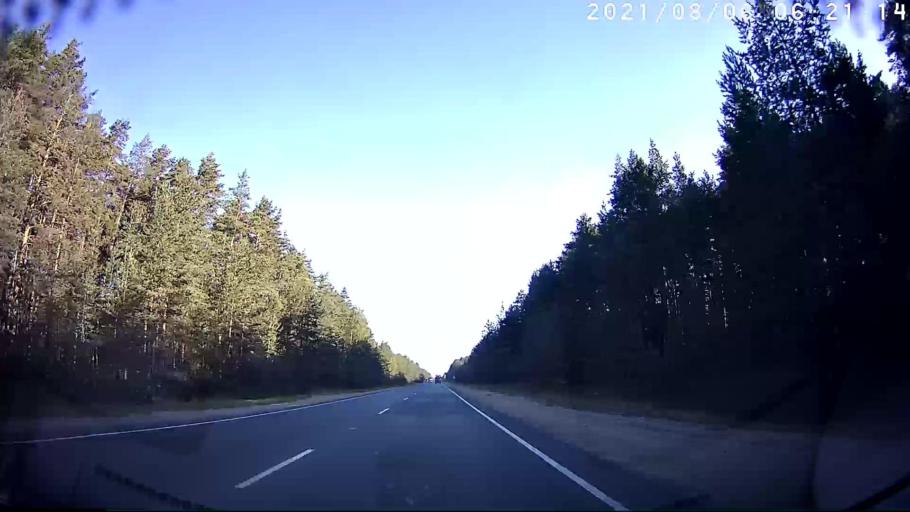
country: RU
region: Mariy-El
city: Krasnogorskiy
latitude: 56.0656
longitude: 48.3670
